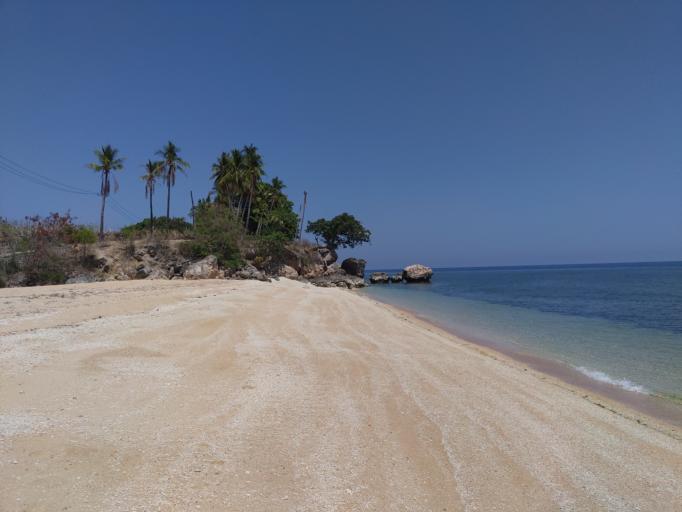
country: TL
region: Baucau
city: Baucau
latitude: -8.4414
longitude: 126.4677
